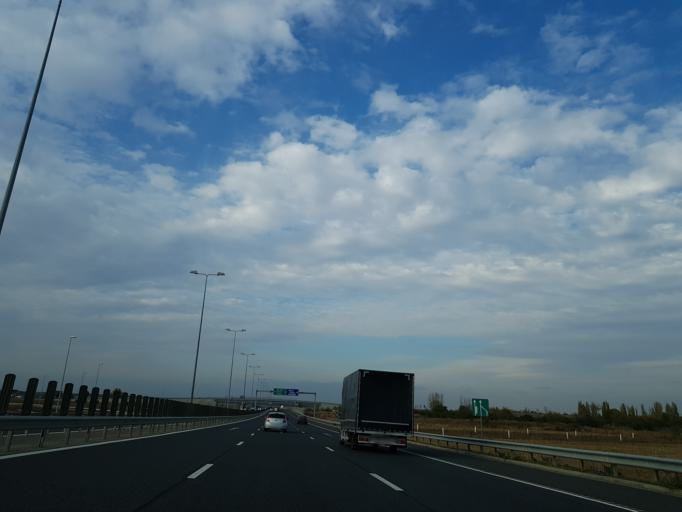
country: RO
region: Ilfov
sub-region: Comuna Moara Vlasiei
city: Caciulati
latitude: 44.6293
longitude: 26.1871
